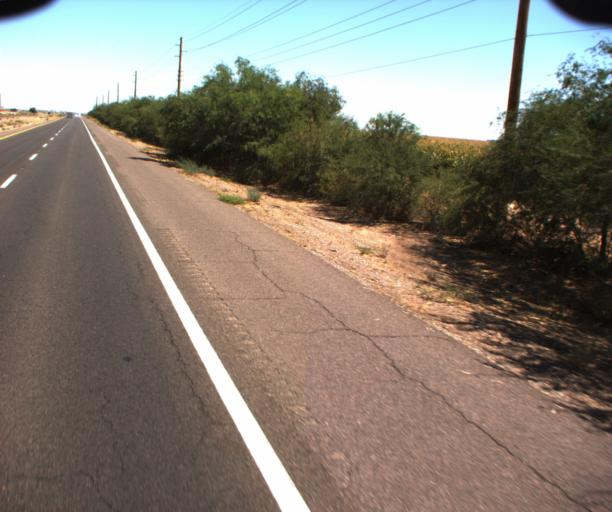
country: US
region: Arizona
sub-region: Pinal County
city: Maricopa
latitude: 32.9799
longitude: -112.0477
